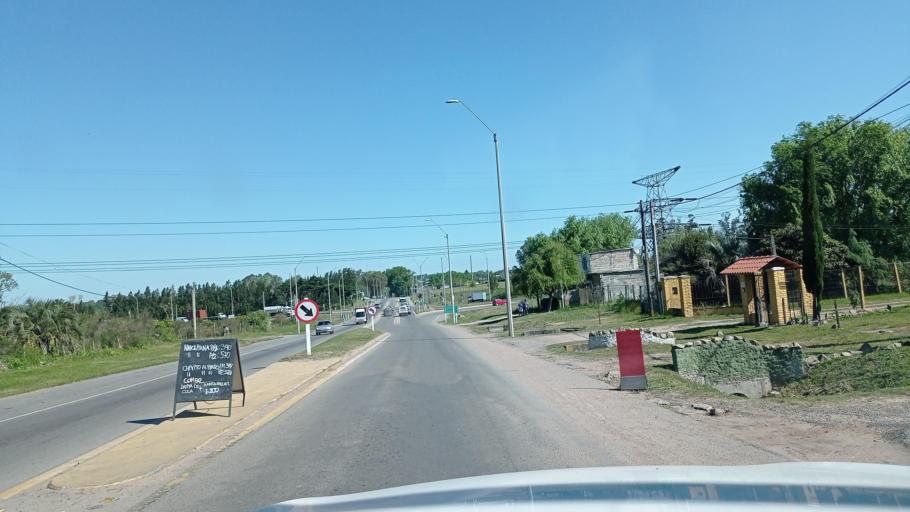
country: UY
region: Canelones
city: La Paz
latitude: -34.7932
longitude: -56.1652
